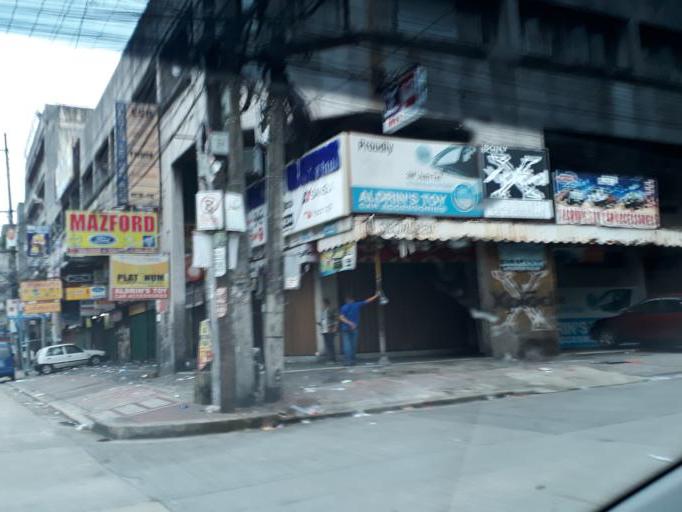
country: PH
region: Calabarzon
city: Del Monte
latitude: 14.6203
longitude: 121.0096
